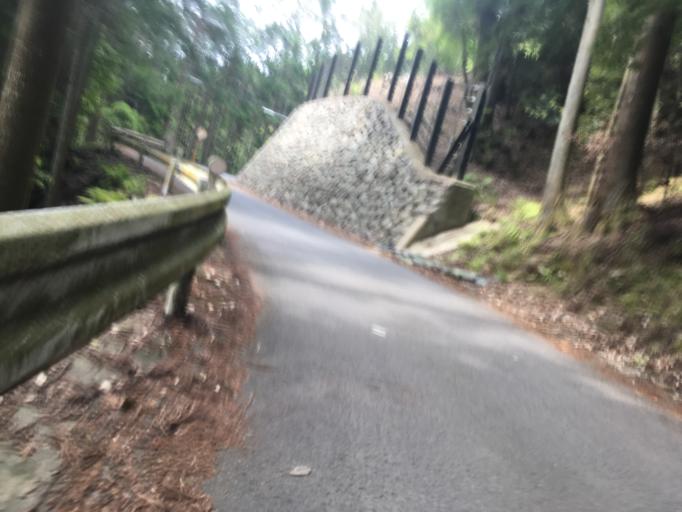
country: JP
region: Kyoto
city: Kameoka
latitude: 35.0267
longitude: 135.6387
